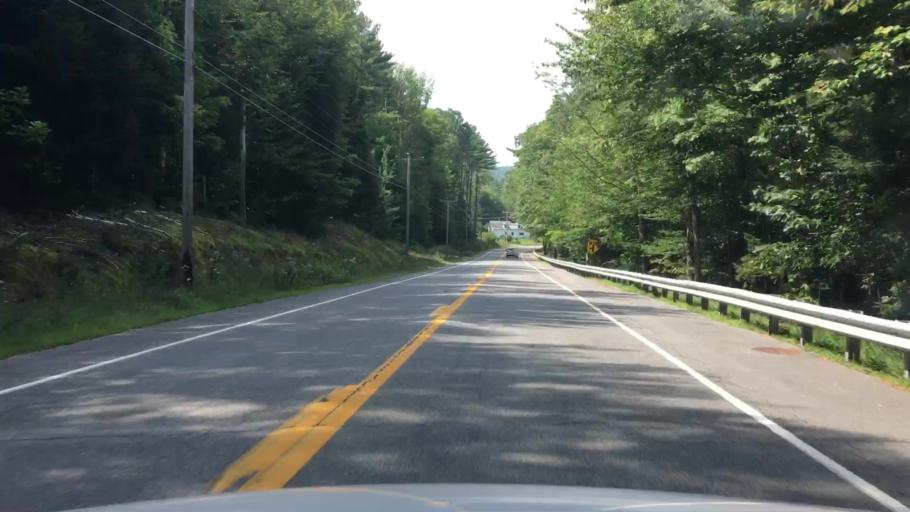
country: US
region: Maine
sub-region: Oxford County
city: Dixfield
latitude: 44.5285
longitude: -70.5045
